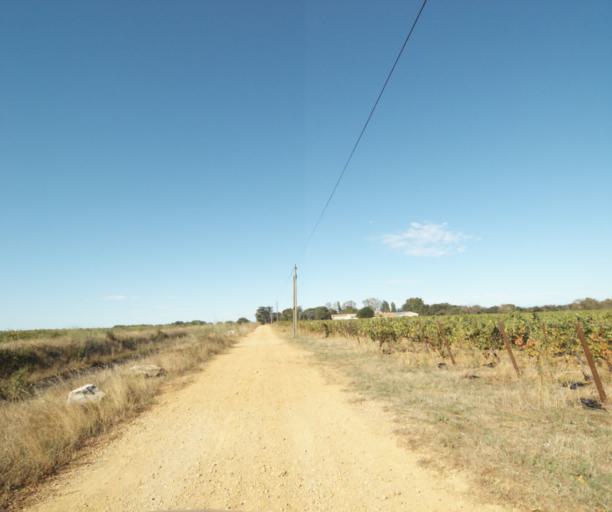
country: FR
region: Languedoc-Roussillon
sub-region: Departement du Gard
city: Bouillargues
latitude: 43.7882
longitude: 4.4126
